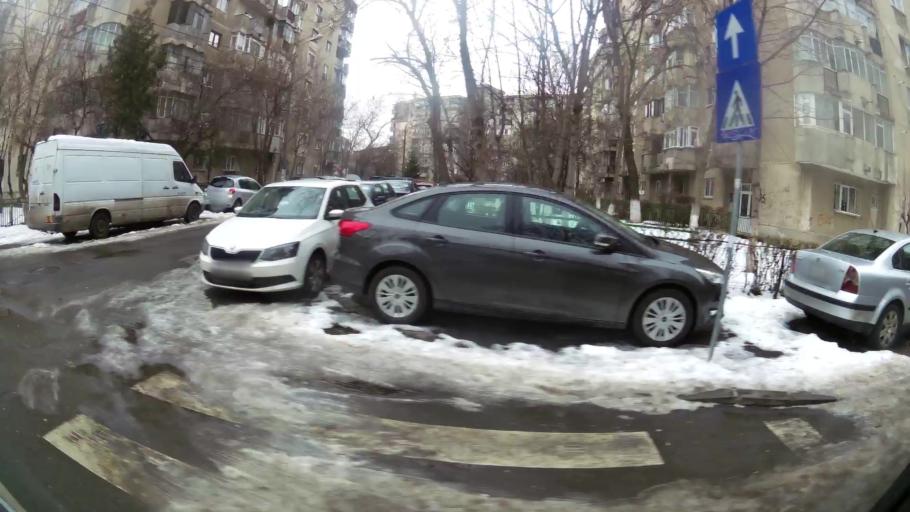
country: RO
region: Bucuresti
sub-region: Municipiul Bucuresti
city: Bucuresti
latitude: 44.4178
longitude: 26.0610
